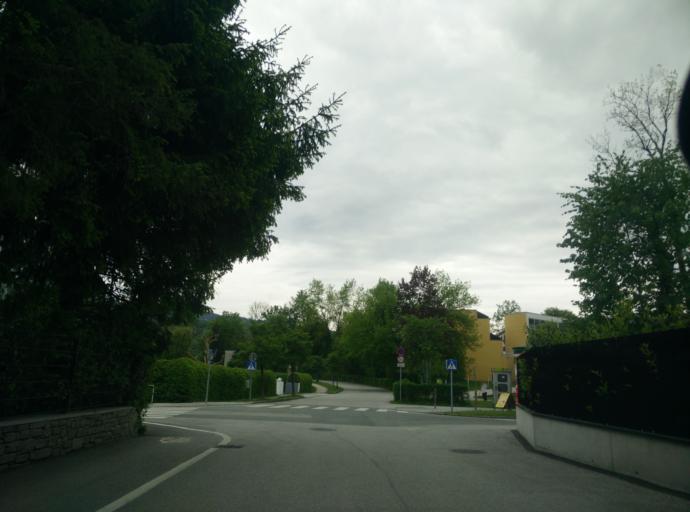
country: AT
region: Salzburg
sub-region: Salzburg Stadt
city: Salzburg
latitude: 47.7952
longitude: 13.0798
